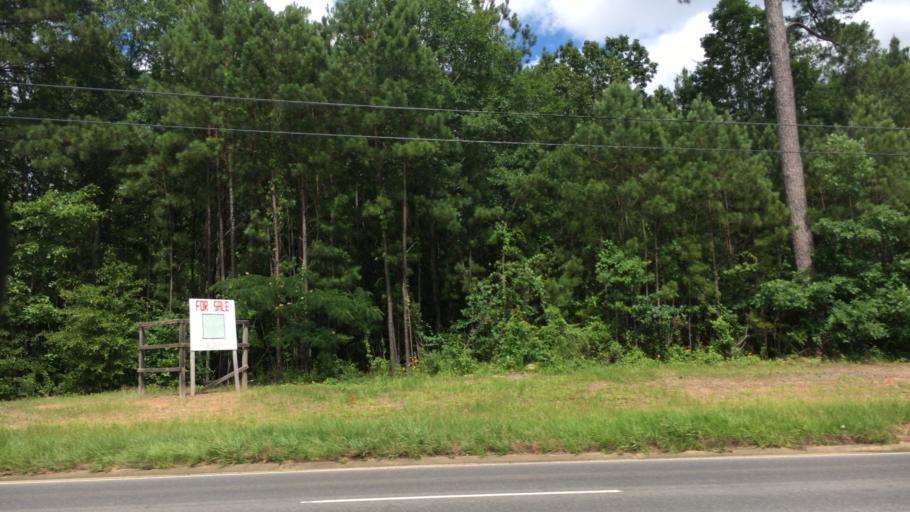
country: US
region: Louisiana
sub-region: Lincoln Parish
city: Ruston
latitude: 32.5017
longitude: -92.6370
